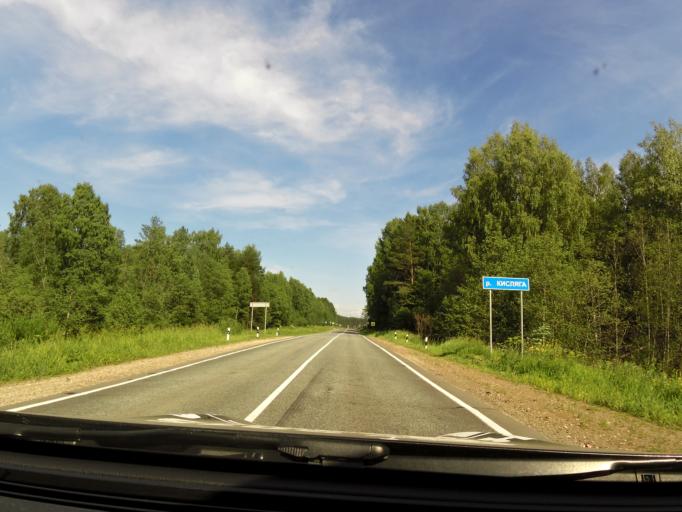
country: RU
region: Kirov
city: Belaya Kholunitsa
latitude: 58.8295
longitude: 50.6518
